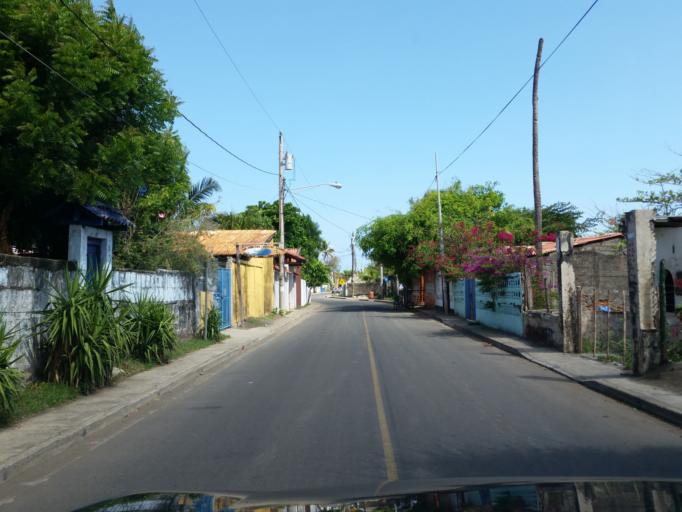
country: NI
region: Leon
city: Leon
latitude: 12.3584
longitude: -87.0204
